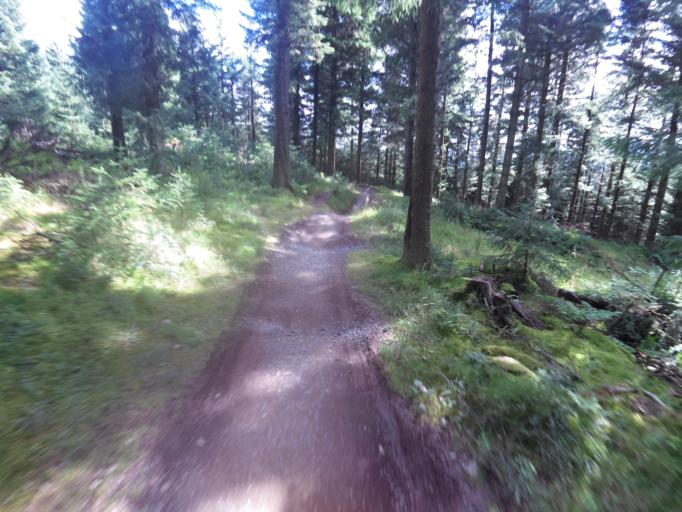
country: GB
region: Scotland
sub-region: The Scottish Borders
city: Peebles
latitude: 55.6674
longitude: -3.1296
